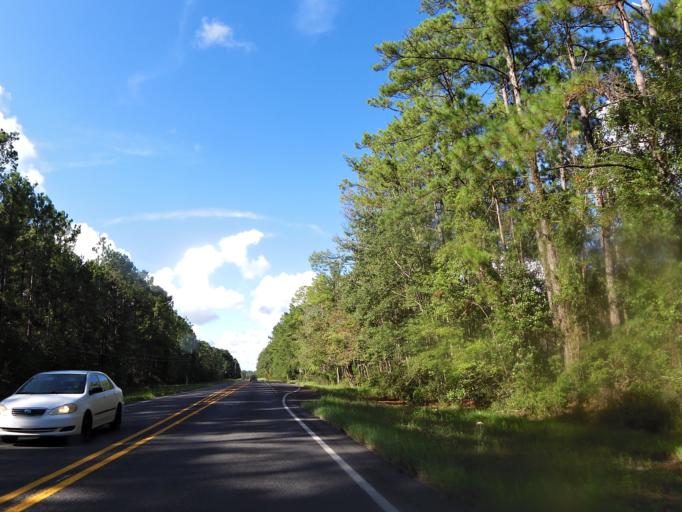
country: US
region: Georgia
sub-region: Camden County
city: Woodbine
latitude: 31.0671
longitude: -81.7283
